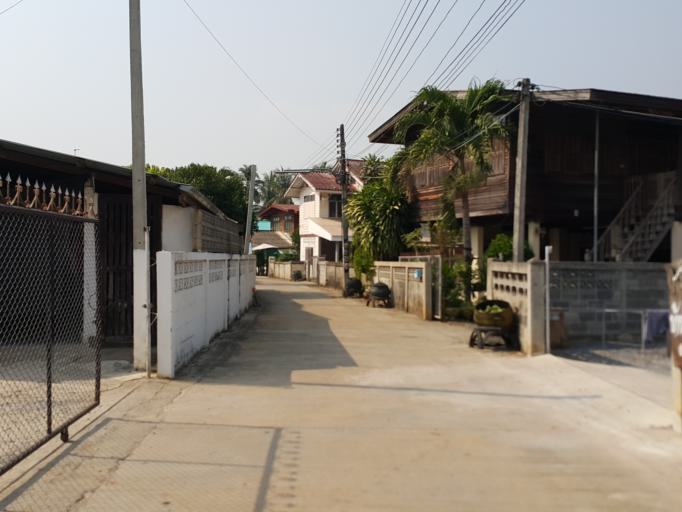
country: TH
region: Sukhothai
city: Thung Saliam
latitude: 17.3282
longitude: 99.5324
